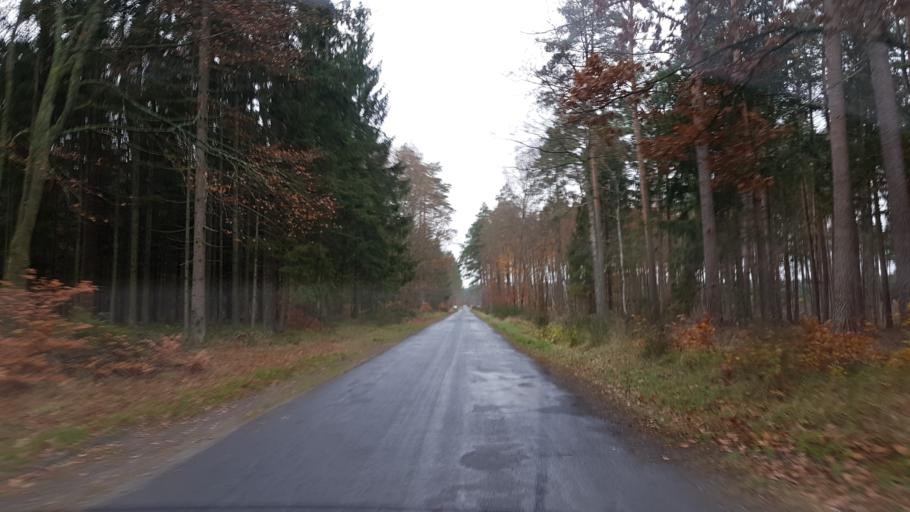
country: PL
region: West Pomeranian Voivodeship
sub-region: Powiat koszalinski
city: Bobolice
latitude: 54.0738
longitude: 16.5738
